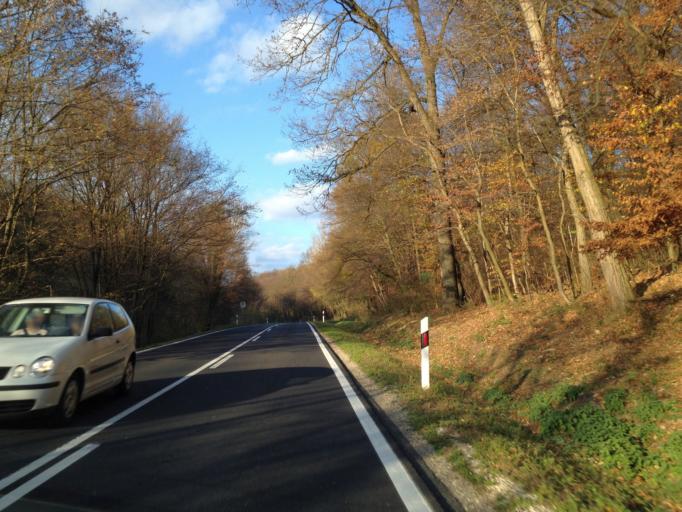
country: HU
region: Gyor-Moson-Sopron
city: Bakonyszentlaszlo
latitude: 47.4020
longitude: 17.8546
